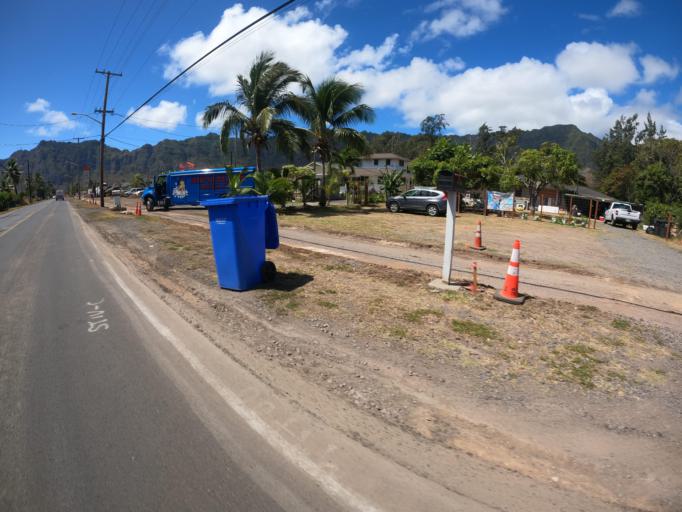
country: US
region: Hawaii
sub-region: Honolulu County
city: Waimanalo Beach
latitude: 21.3398
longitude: -157.7039
